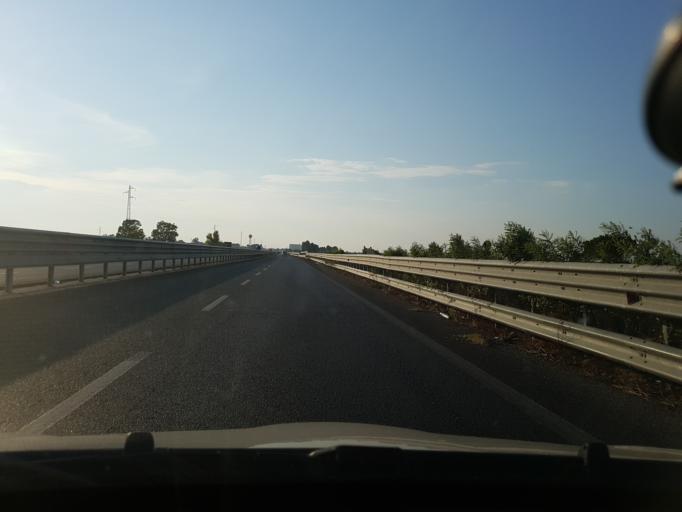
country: IT
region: Apulia
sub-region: Provincia di Foggia
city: Carapelle
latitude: 41.3844
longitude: 15.6728
